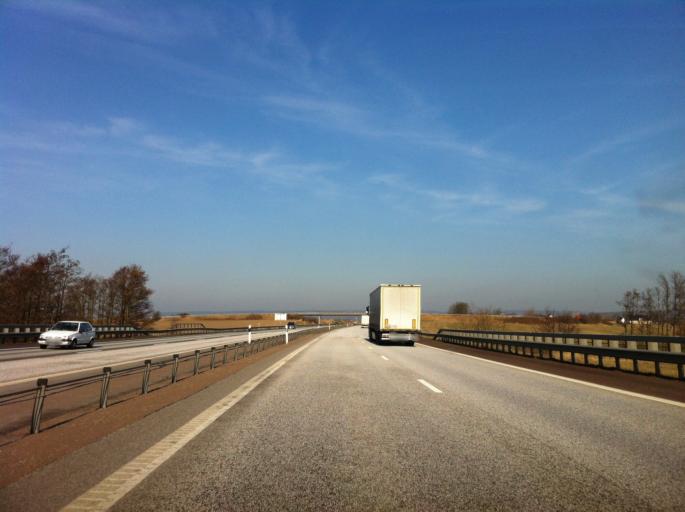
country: SE
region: Skane
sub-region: Angelholms Kommun
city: AEngelholm
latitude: 56.2677
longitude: 12.8938
